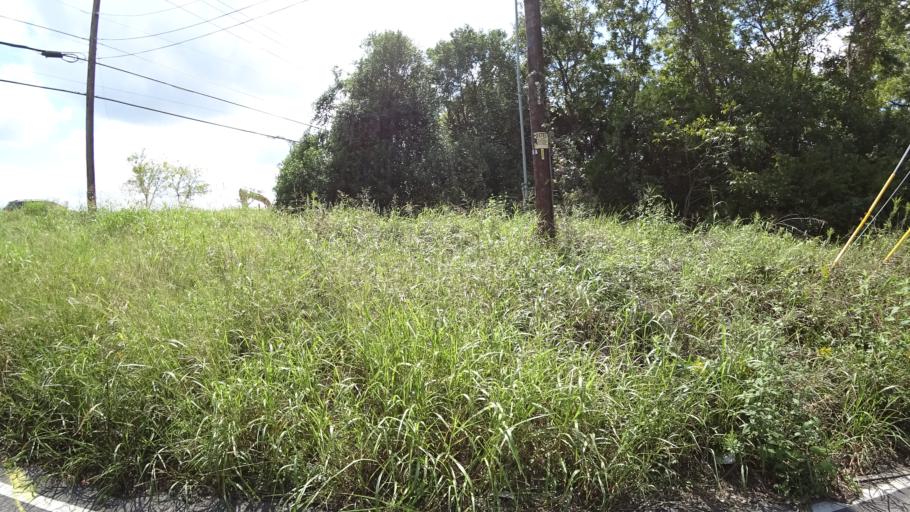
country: US
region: Texas
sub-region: Travis County
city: Onion Creek
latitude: 30.1833
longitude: -97.7824
